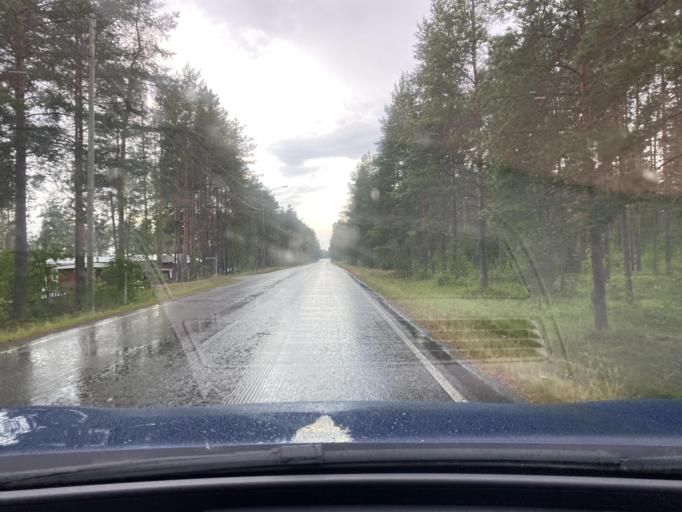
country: FI
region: Central Ostrobothnia
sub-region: Kaustinen
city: Veteli
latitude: 63.4696
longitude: 23.8193
